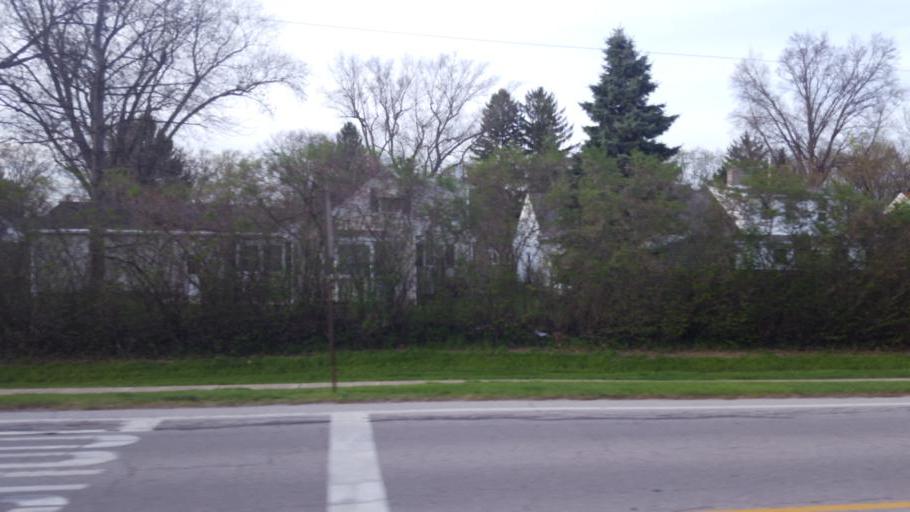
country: US
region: Ohio
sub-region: Erie County
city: Huron
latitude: 41.3881
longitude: -82.5367
